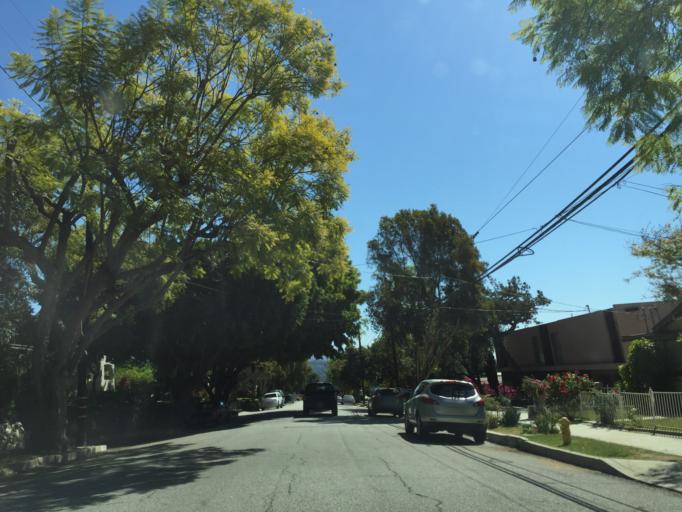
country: US
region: California
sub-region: Los Angeles County
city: Sierra Madre
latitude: 34.1644
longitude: -118.0500
